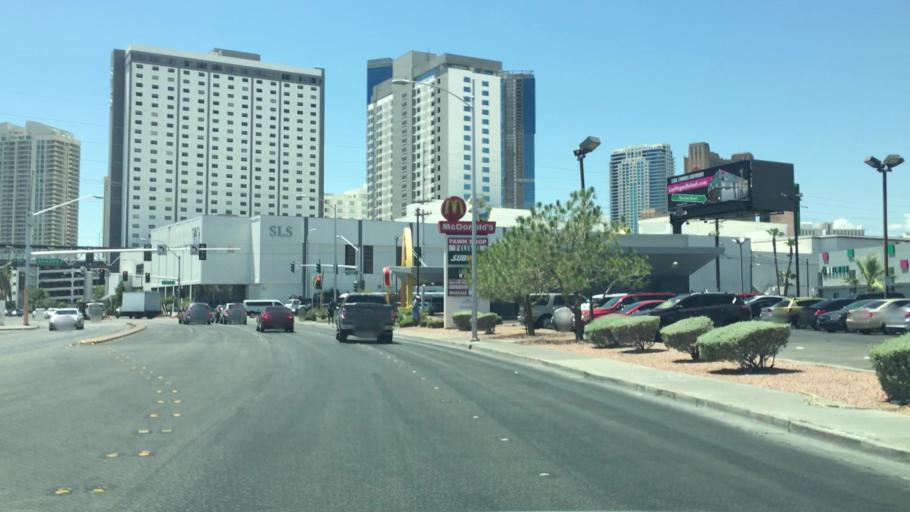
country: US
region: Nevada
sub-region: Clark County
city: Las Vegas
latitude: 36.1446
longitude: -115.1546
